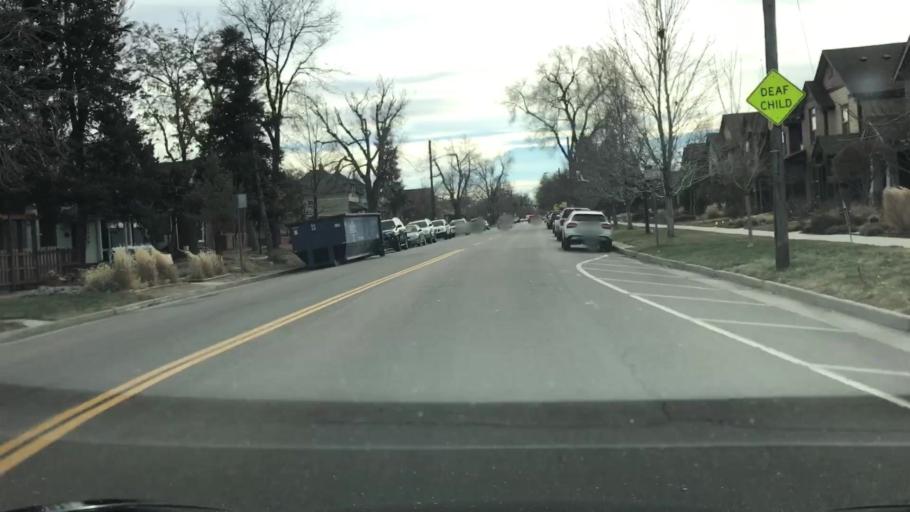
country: US
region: Colorado
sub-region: Denver County
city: Denver
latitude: 39.6962
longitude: -104.9828
